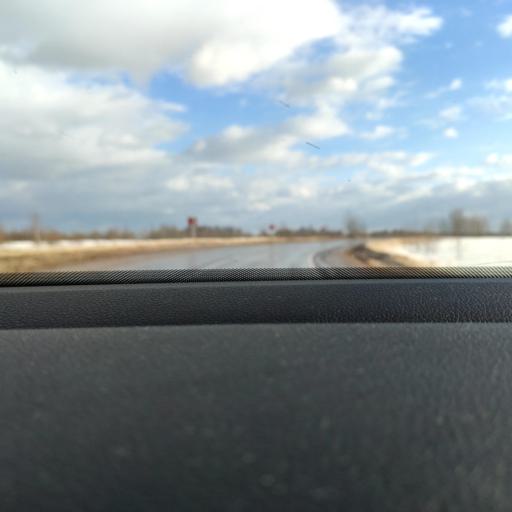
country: RU
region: Moskovskaya
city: Istra
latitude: 56.0229
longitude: 36.8118
